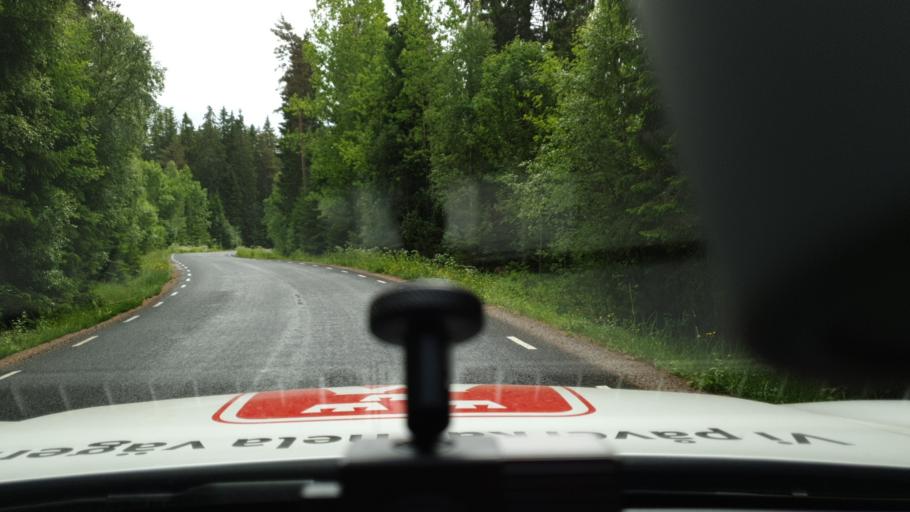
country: SE
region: Joenkoeping
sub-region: Mullsjo Kommun
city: Mullsjoe
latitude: 57.9991
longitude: 13.7306
